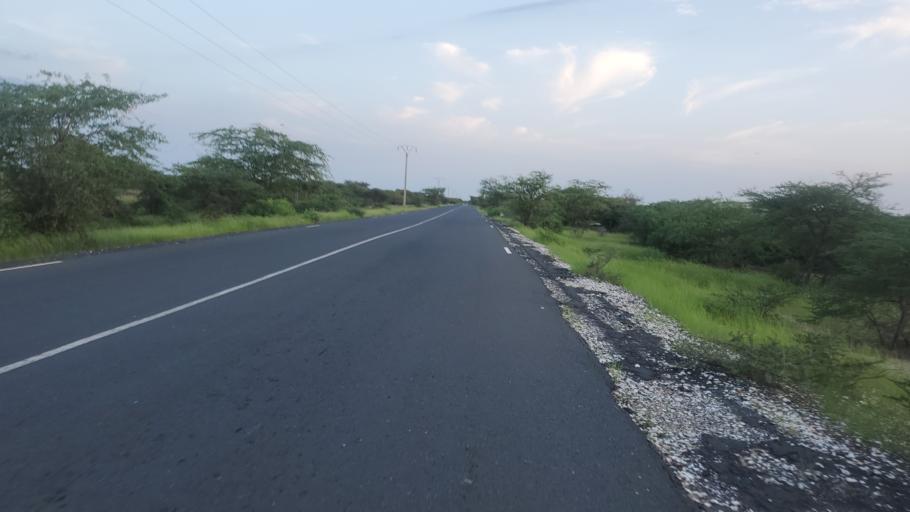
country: SN
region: Saint-Louis
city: Saint-Louis
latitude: 16.1181
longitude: -16.4142
